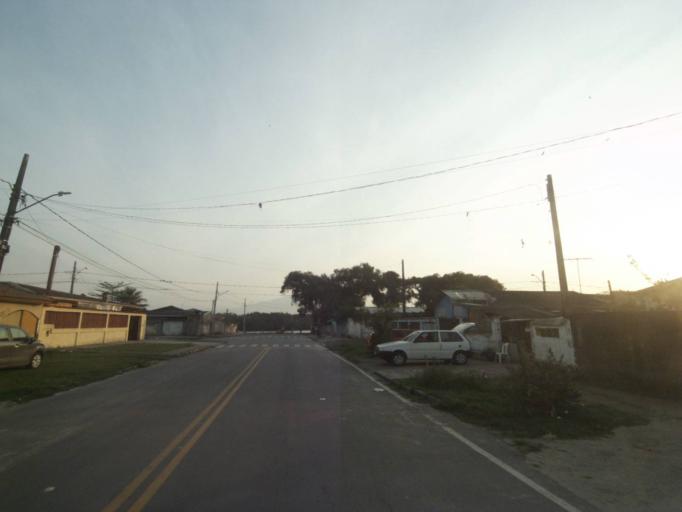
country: BR
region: Parana
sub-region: Paranagua
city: Paranagua
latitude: -25.5174
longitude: -48.5457
